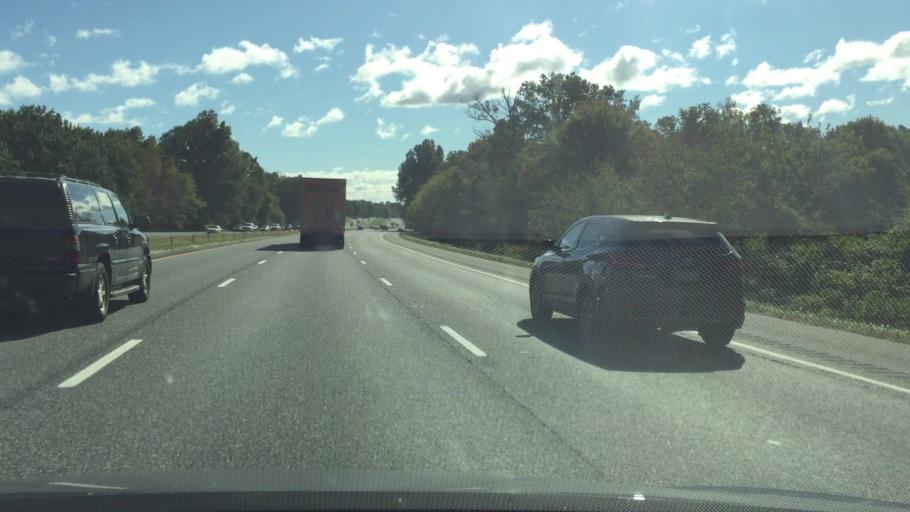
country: US
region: Maryland
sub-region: Carroll County
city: Sykesville
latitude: 39.3210
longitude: -76.9910
